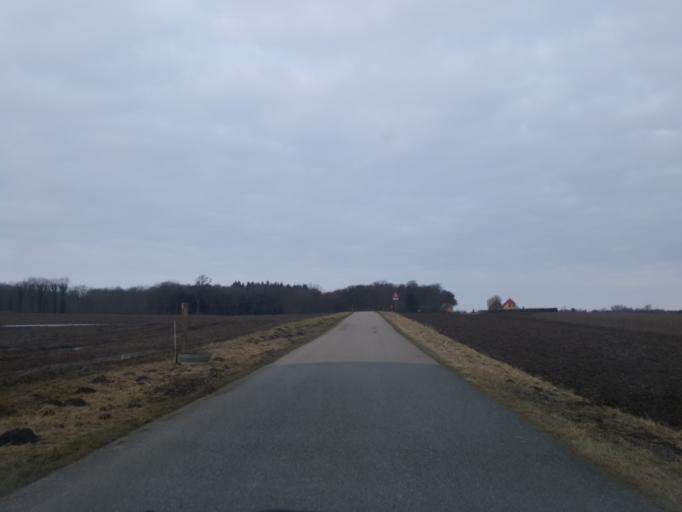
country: DK
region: Zealand
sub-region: Vordingborg Kommune
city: Neder Vindinge
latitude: 55.0309
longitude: 11.8497
